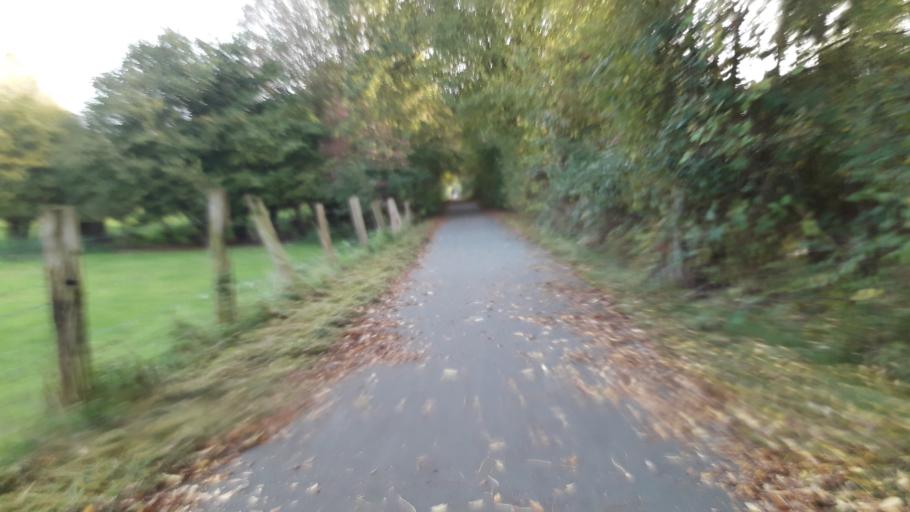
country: DE
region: North Rhine-Westphalia
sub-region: Regierungsbezirk Detmold
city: Paderborn
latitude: 51.6827
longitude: 8.6979
